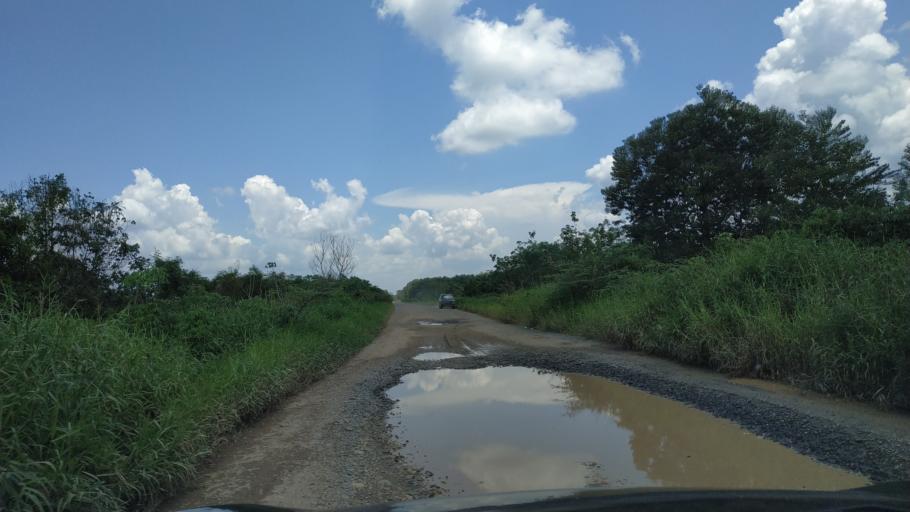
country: ID
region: Riau
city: Pangkalanbunut
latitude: 0.1963
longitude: 102.3880
